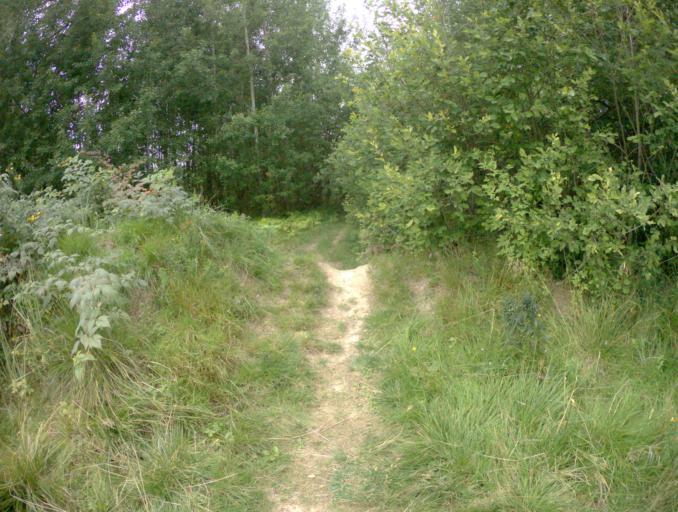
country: RU
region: Vladimir
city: Raduzhnyy
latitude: 56.0084
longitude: 40.3239
